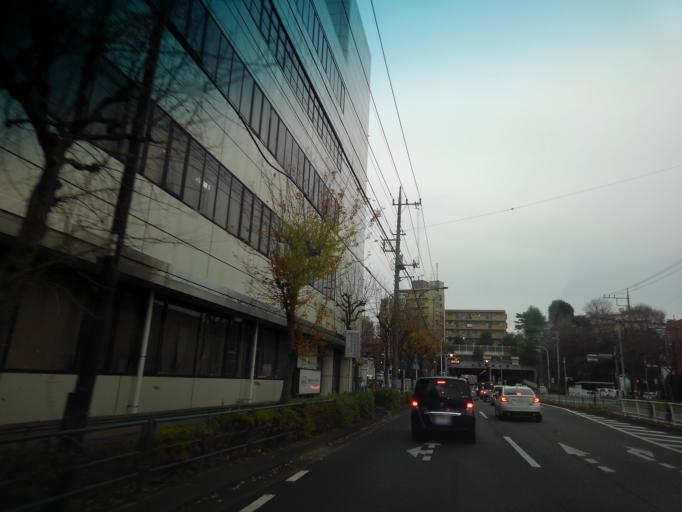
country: JP
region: Tokyo
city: Kokubunji
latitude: 35.6671
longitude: 139.4592
